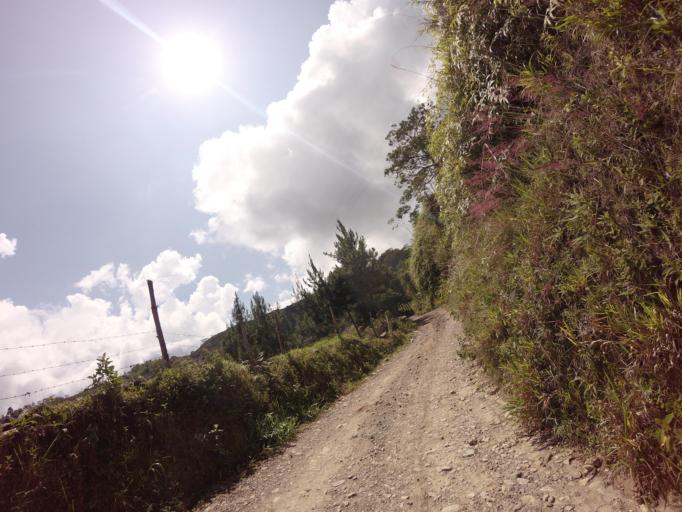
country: CO
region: Caldas
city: Pensilvania
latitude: 5.4919
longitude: -75.1841
